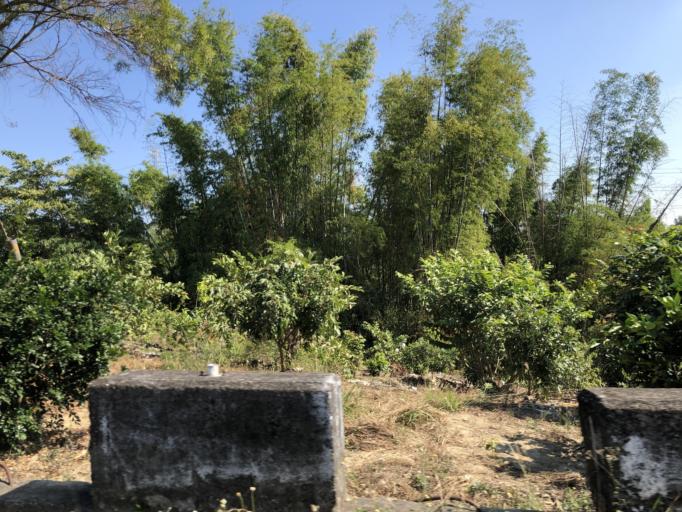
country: TW
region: Taiwan
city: Yujing
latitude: 23.0416
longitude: 120.3623
